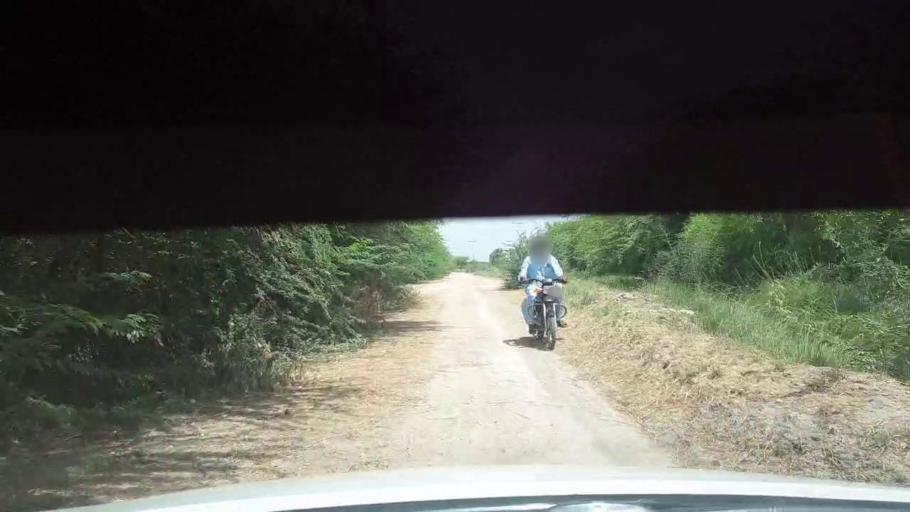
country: PK
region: Sindh
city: Kadhan
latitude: 24.5145
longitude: 68.9735
